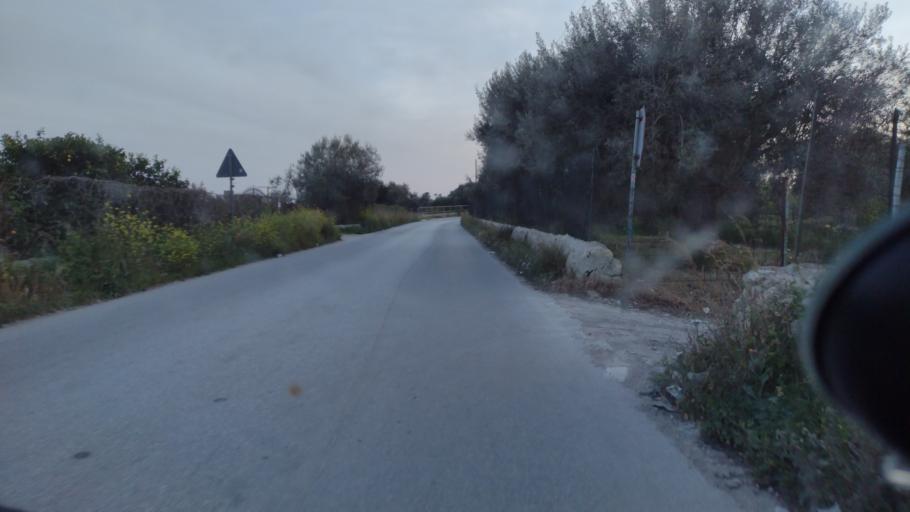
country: IT
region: Sicily
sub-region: Provincia di Siracusa
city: Avola
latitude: 36.8915
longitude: 15.1329
